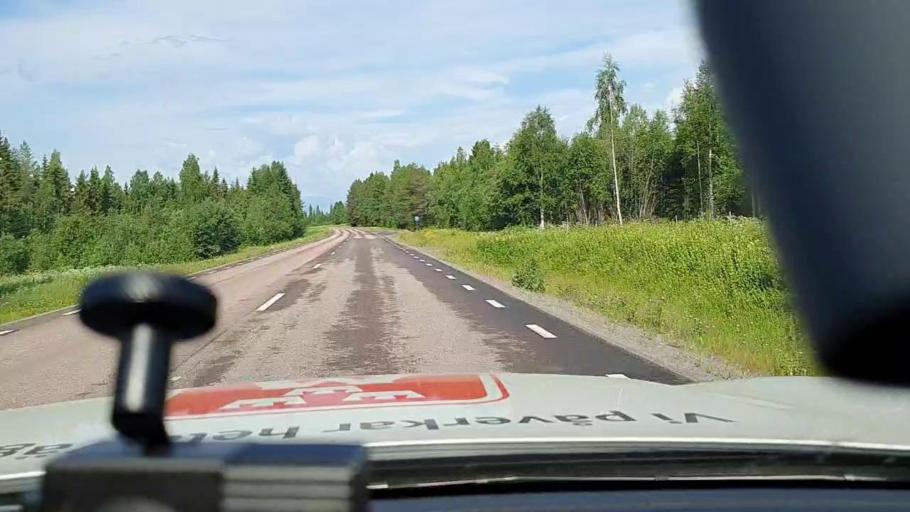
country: SE
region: Norrbotten
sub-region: Alvsbyns Kommun
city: AElvsbyn
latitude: 66.0212
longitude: 21.1344
